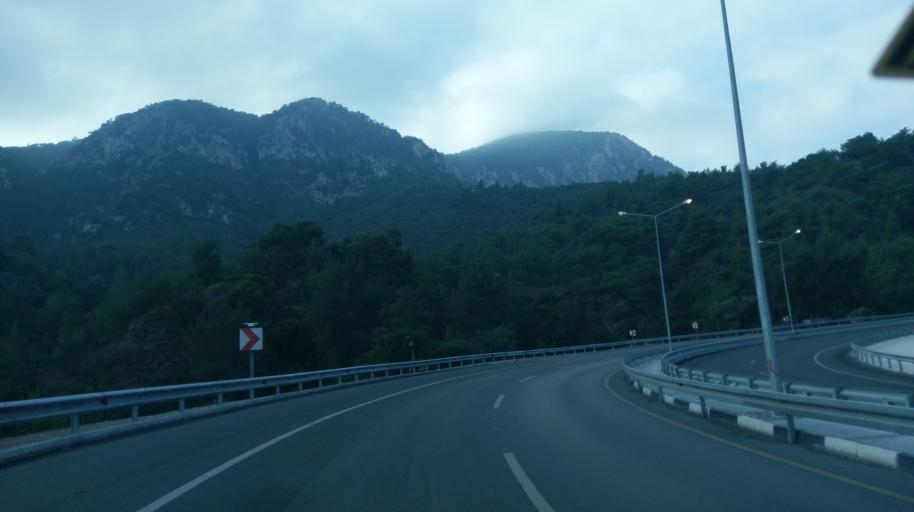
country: CY
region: Keryneia
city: Kyrenia
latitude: 35.3075
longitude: 33.3222
